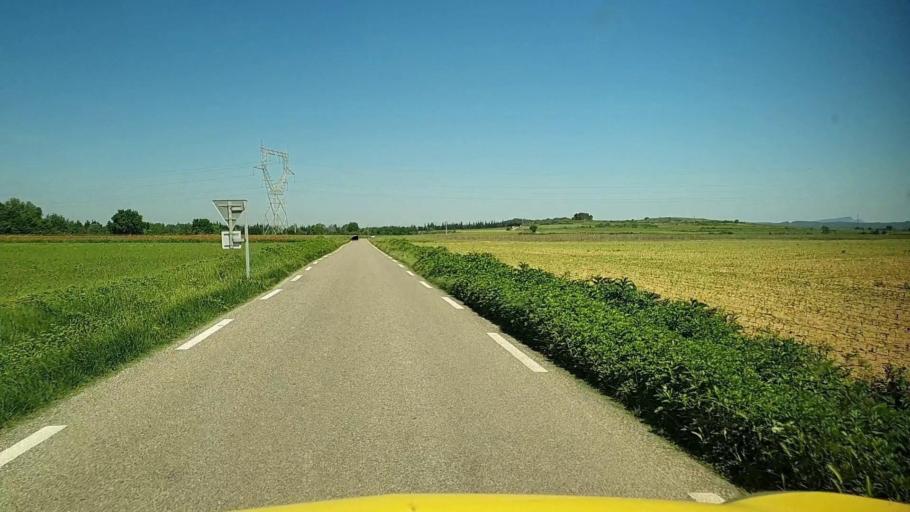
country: FR
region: Languedoc-Roussillon
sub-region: Departement du Gard
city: Saint-Chaptes
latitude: 43.9421
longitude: 4.3122
